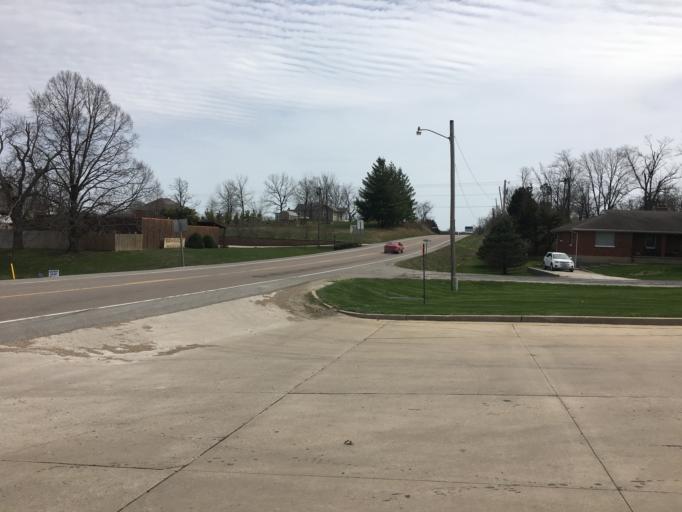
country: US
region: Missouri
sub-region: Osage County
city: Linn
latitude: 38.4711
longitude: -91.8325
